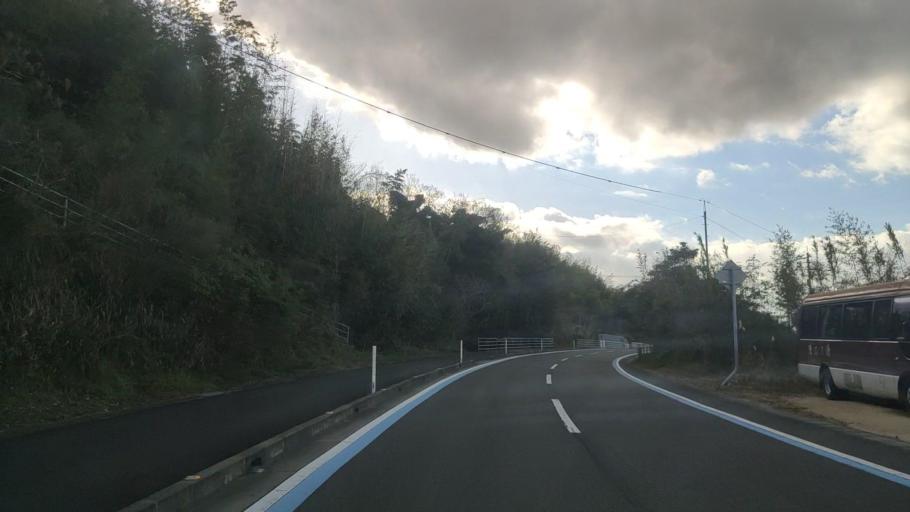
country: JP
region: Hiroshima
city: Innoshima
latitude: 34.2302
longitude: 133.0821
